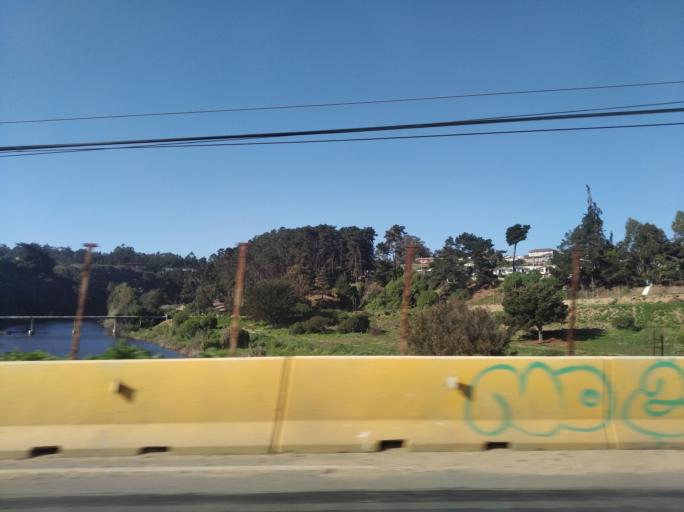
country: CL
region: Valparaiso
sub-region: San Antonio Province
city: El Tabo
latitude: -33.4457
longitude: -71.6784
